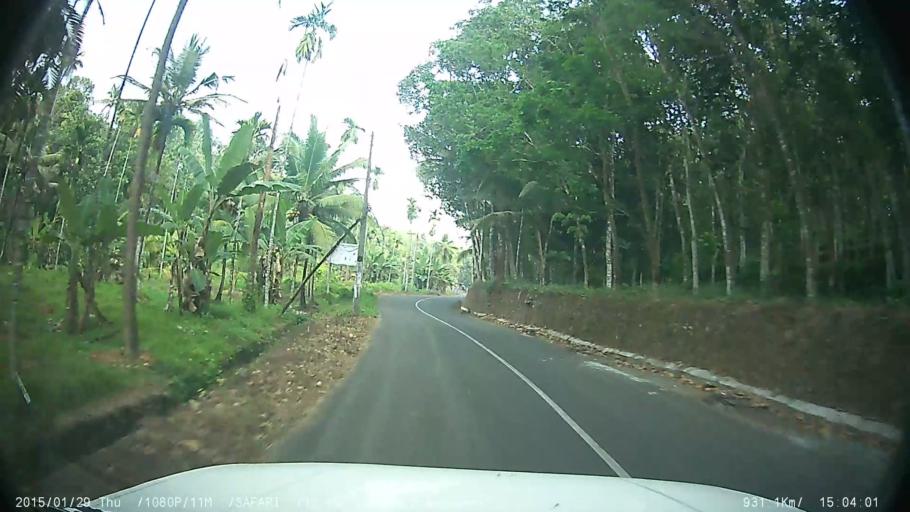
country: IN
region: Kerala
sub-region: Kottayam
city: Palackattumala
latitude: 9.7280
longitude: 76.5856
